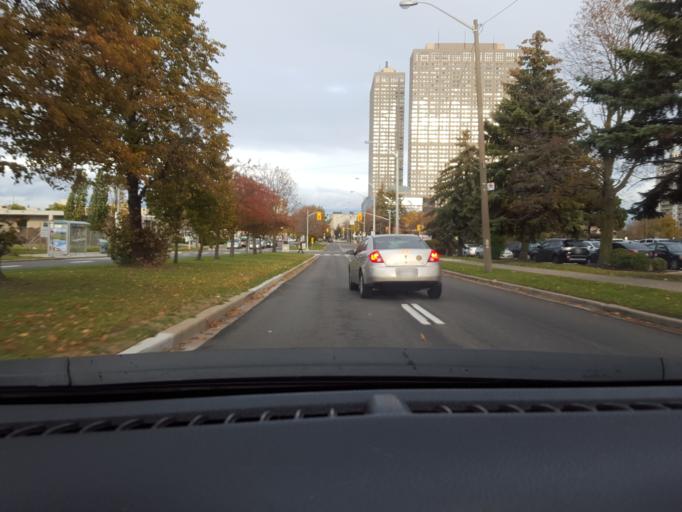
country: CA
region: Ontario
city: Toronto
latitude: 43.7067
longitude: -79.3468
